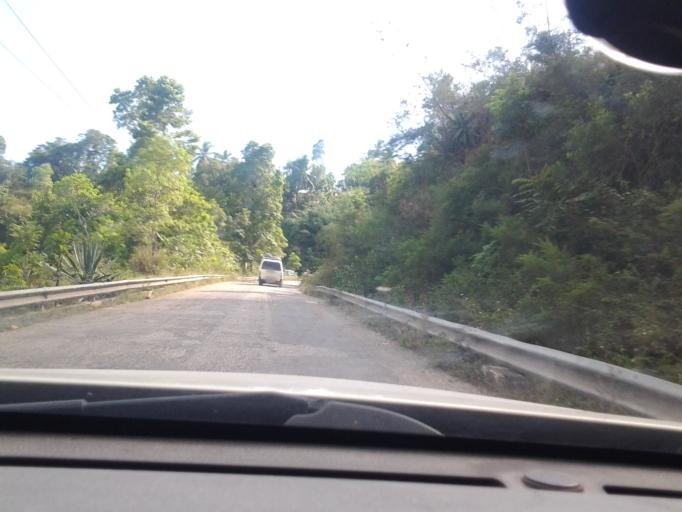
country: HT
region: Sud-Est
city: Jacmel
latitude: 18.3036
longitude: -72.5867
